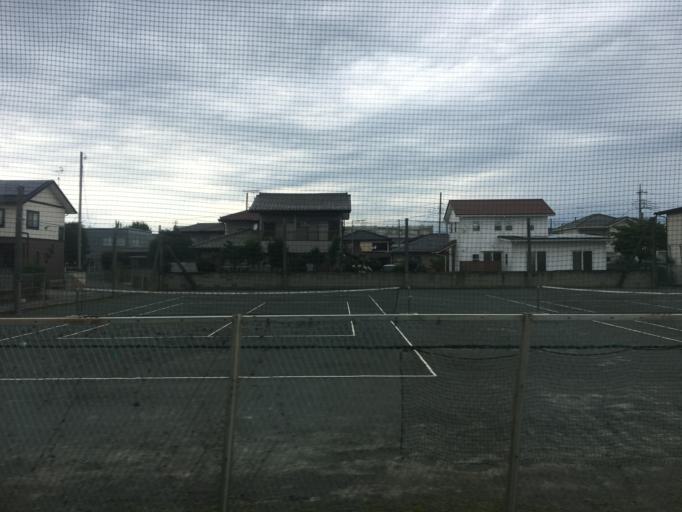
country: JP
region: Gunma
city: Maebashi-shi
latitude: 36.3942
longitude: 139.1034
